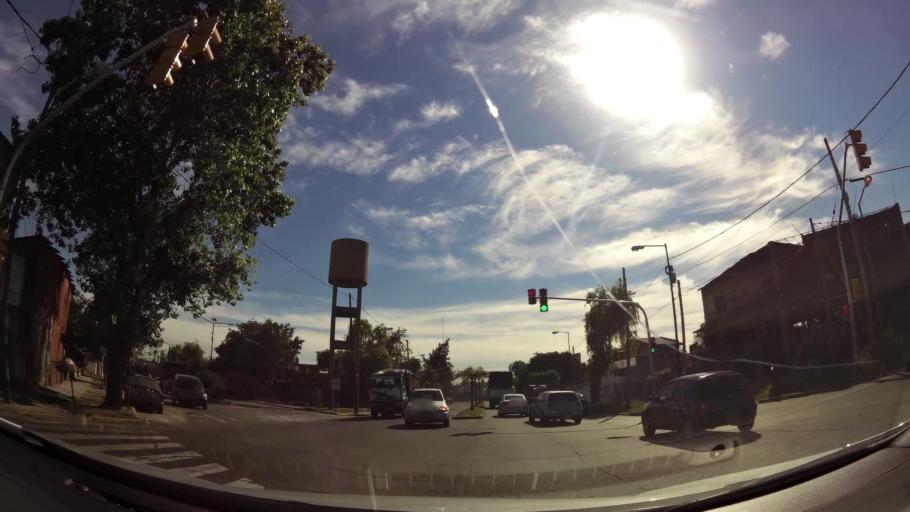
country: AR
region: Buenos Aires
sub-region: Partido de Tigre
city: Tigre
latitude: -34.4780
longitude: -58.5804
